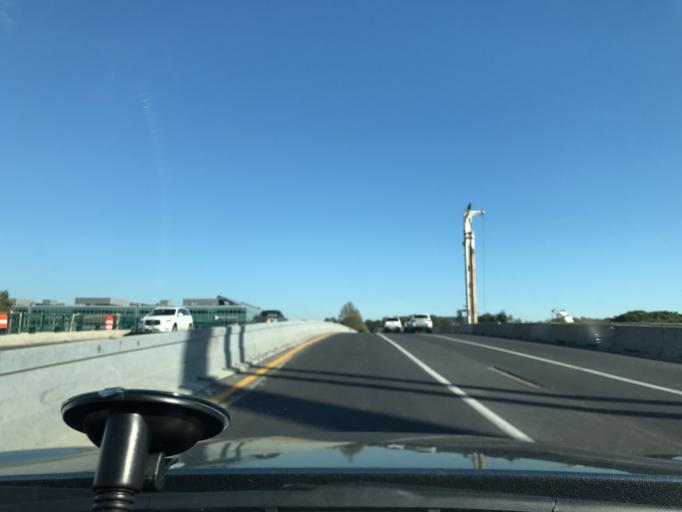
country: US
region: Massachusetts
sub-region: Middlesex County
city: Everett
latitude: 42.4040
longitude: -71.0733
